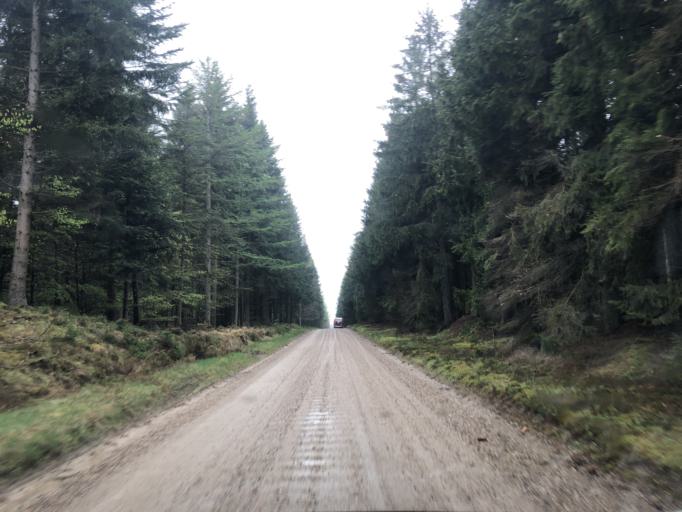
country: DK
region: Central Jutland
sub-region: Lemvig Kommune
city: Lemvig
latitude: 56.4649
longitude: 8.3952
